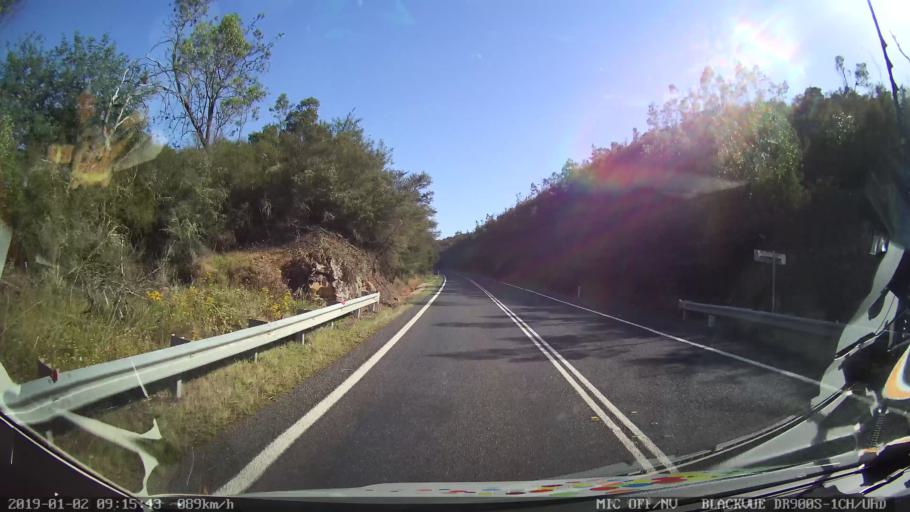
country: AU
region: New South Wales
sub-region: Tumut Shire
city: Tumut
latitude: -35.4618
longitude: 148.2815
